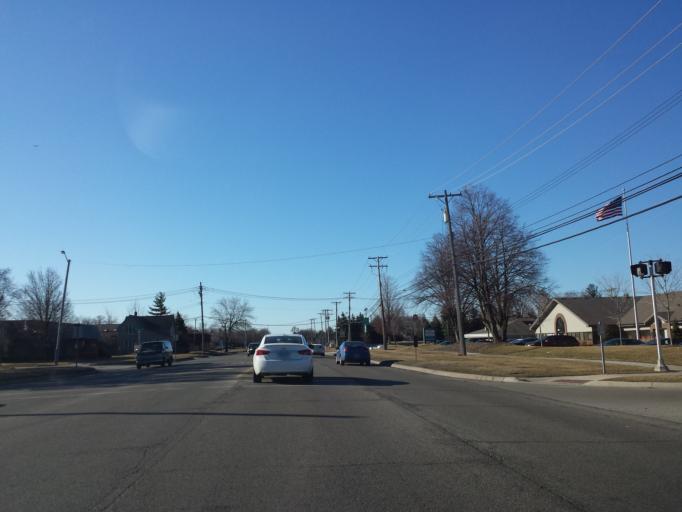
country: US
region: Michigan
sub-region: Oakland County
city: Clawson
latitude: 42.5564
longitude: -83.1474
